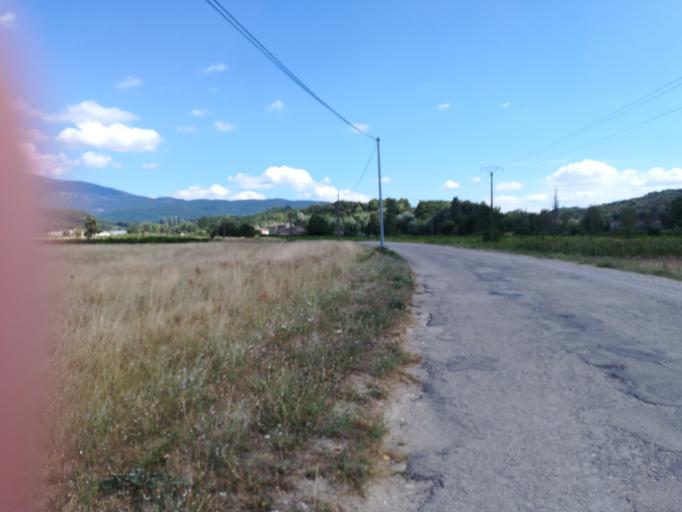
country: FR
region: Provence-Alpes-Cote d'Azur
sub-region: Departement du Vaucluse
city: Vaison-la-Romaine
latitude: 44.2099
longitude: 5.1075
